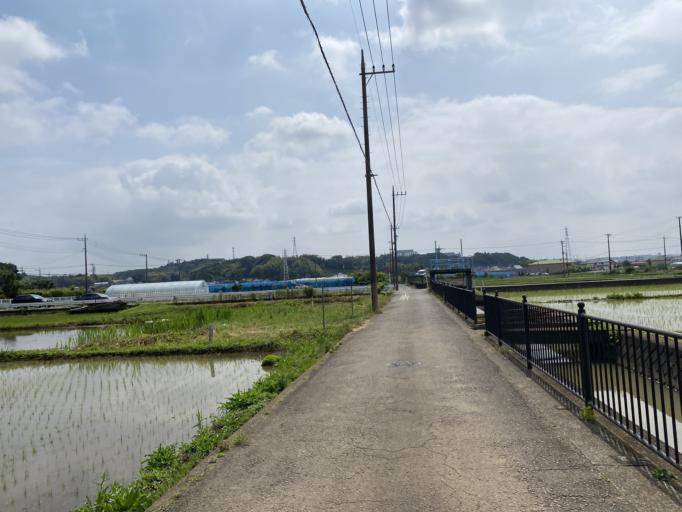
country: JP
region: Tokyo
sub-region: Machida-shi
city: Machida
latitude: 35.5669
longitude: 139.5064
